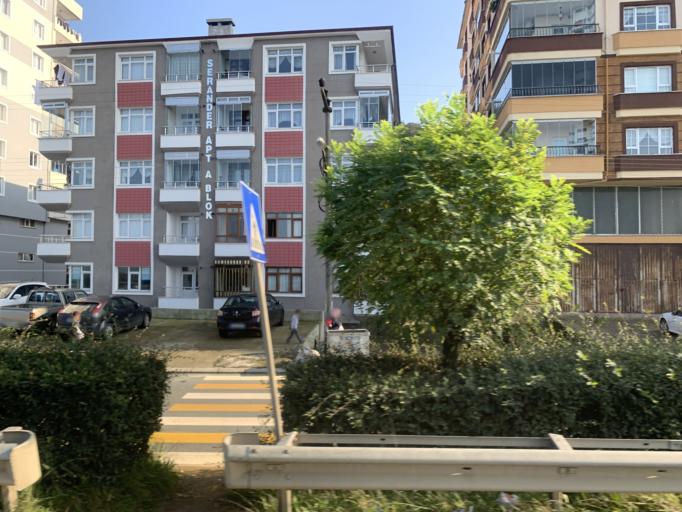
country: TR
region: Trabzon
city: Of
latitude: 40.9402
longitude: 40.2567
